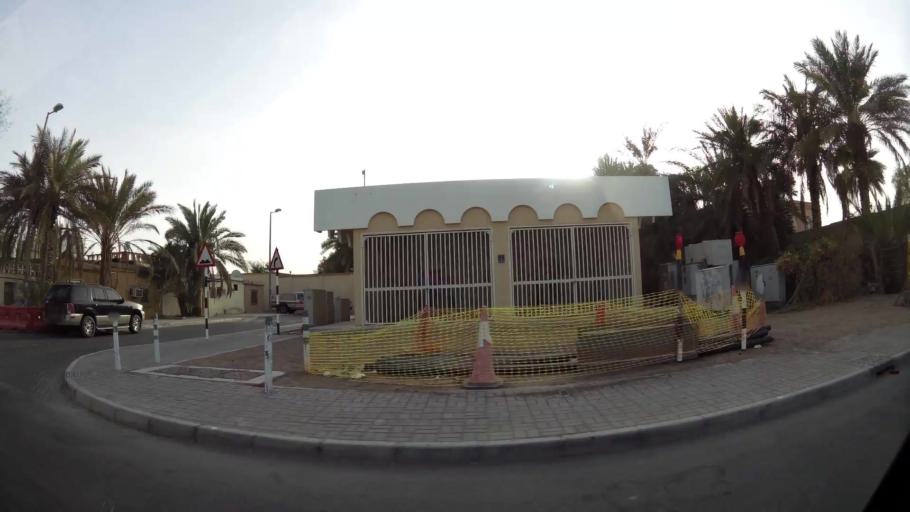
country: OM
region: Al Buraimi
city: Al Buraymi
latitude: 24.2439
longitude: 55.7500
